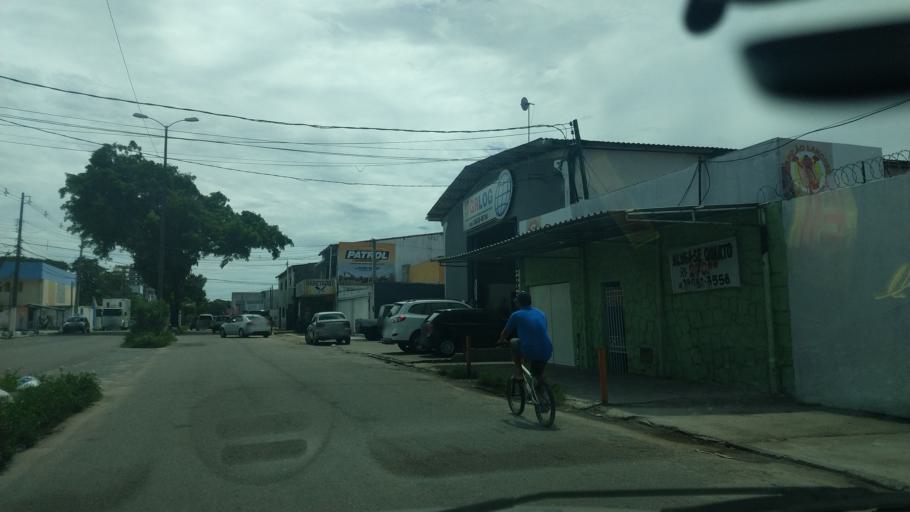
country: BR
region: Rio Grande do Norte
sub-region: Natal
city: Natal
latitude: -5.8262
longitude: -35.2346
